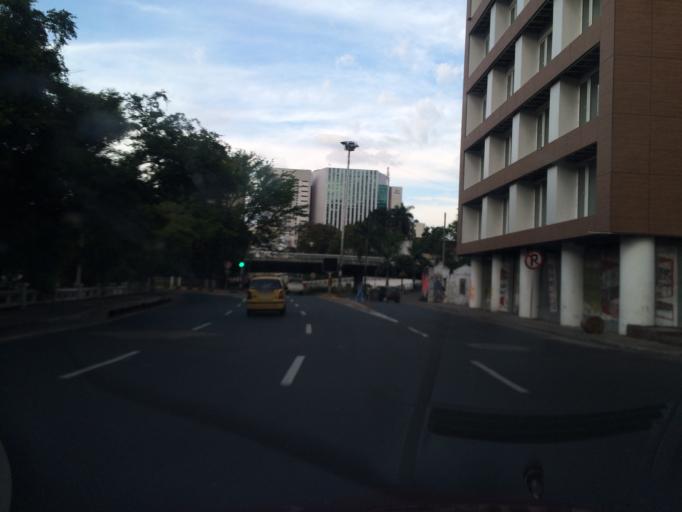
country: CO
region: Valle del Cauca
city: Cali
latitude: 3.4505
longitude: -76.5389
